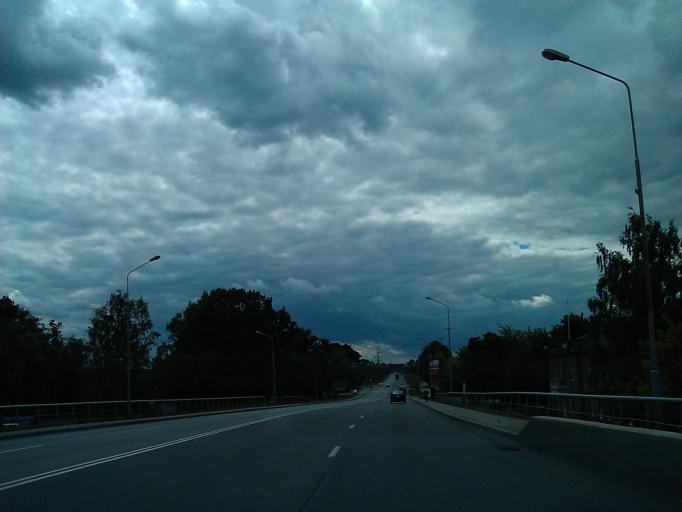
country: LV
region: Jelgava
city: Jelgava
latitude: 56.6380
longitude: 23.7289
